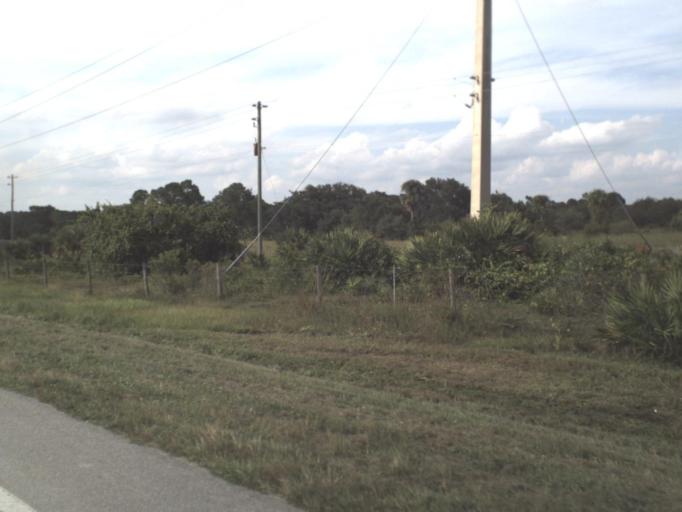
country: US
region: Florida
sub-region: Okeechobee County
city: Taylor Creek
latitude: 27.1711
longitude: -80.6954
